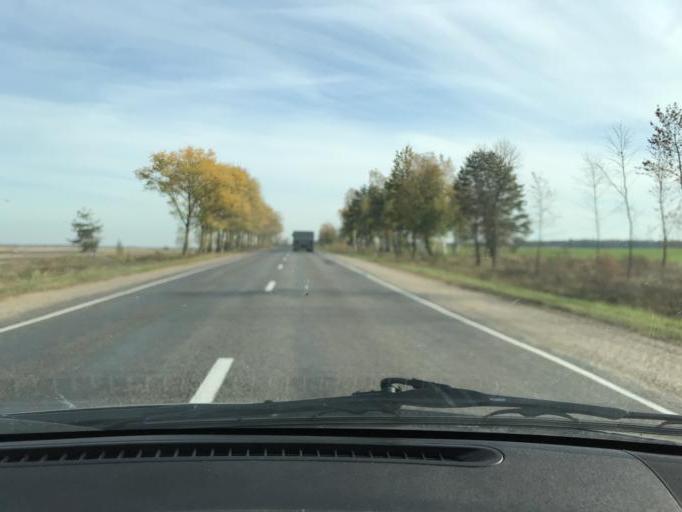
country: BY
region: Brest
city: Lahishyn
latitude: 52.2422
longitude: 25.9980
